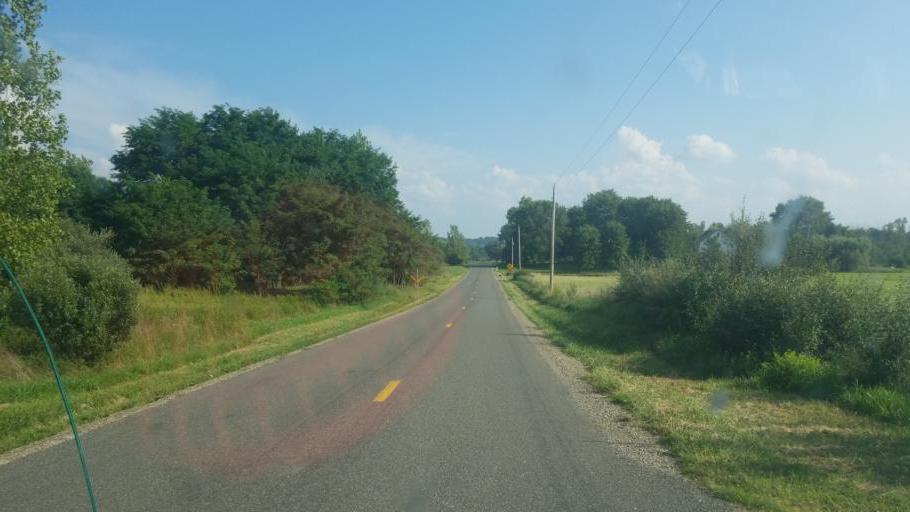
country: US
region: Ohio
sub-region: Medina County
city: Westfield Center
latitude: 41.0009
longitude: -81.9601
